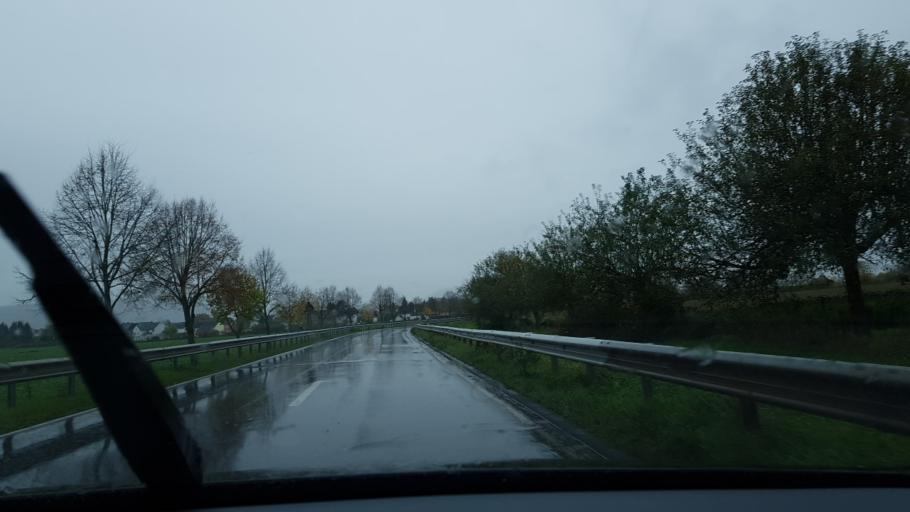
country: DE
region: Rheinland-Pfalz
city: Neuerburg
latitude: 49.9856
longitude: 6.9379
